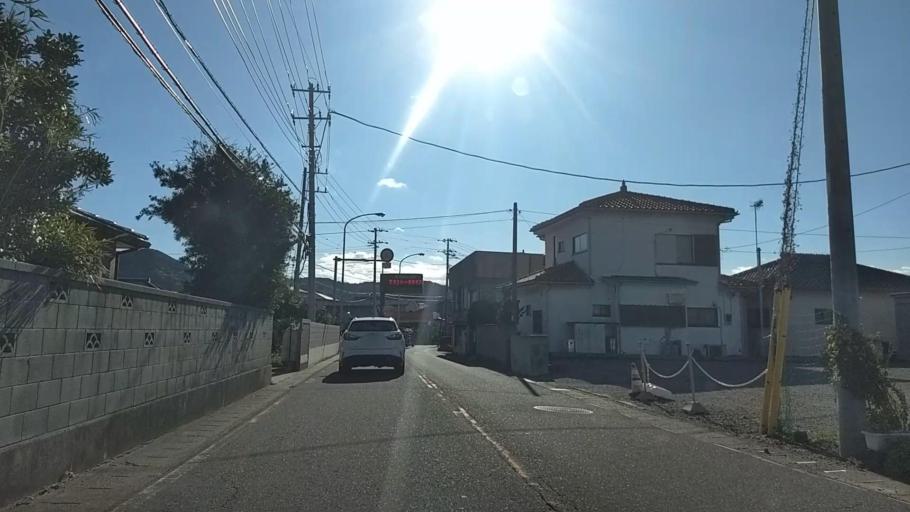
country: JP
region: Chiba
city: Futtsu
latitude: 35.1437
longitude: 139.8351
